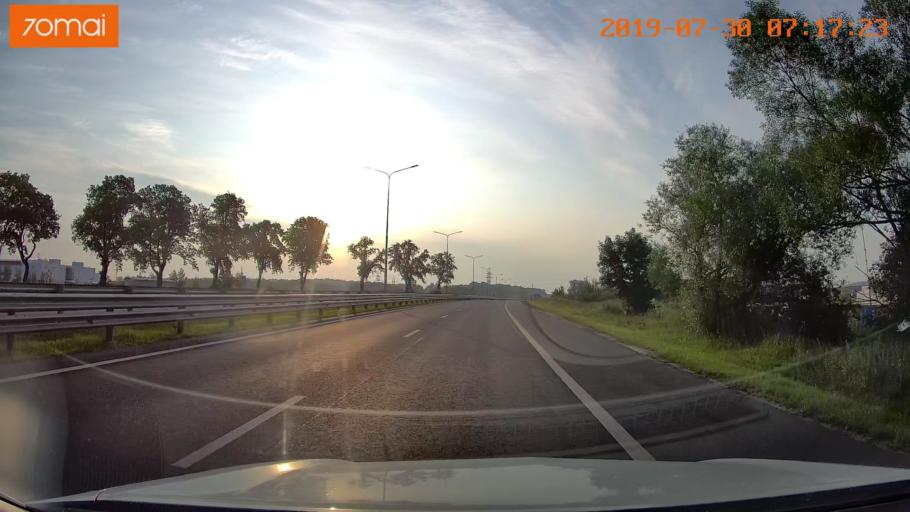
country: RU
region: Kaliningrad
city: Bol'shoe Isakovo
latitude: 54.7073
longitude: 20.6260
